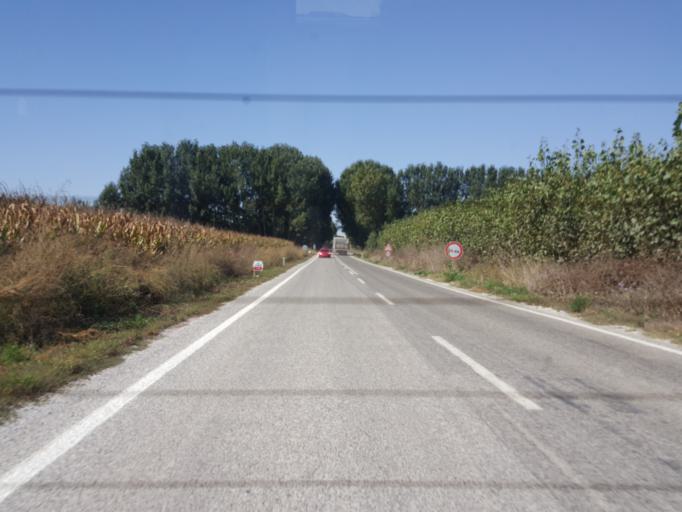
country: TR
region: Tokat
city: Pazar
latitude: 40.2679
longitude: 36.1969
